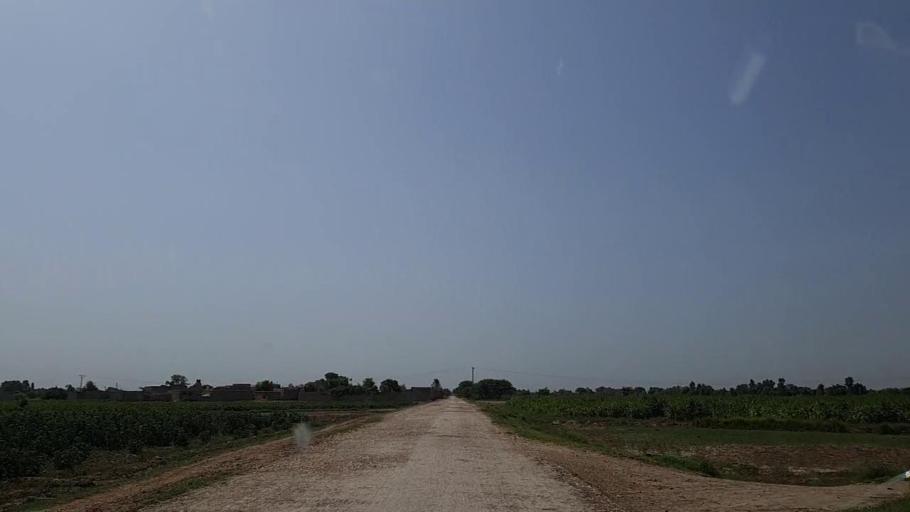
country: PK
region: Sindh
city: Naushahro Firoz
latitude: 26.8516
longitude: 68.0096
